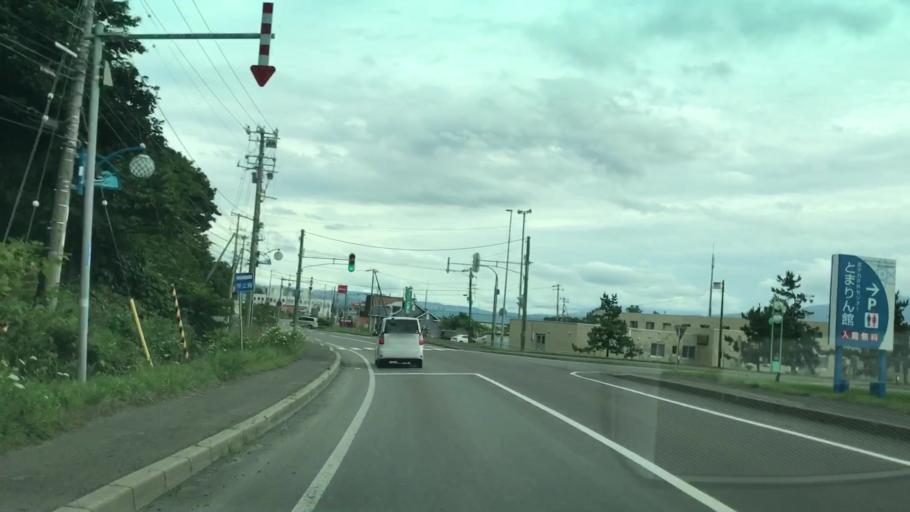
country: JP
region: Hokkaido
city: Iwanai
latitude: 43.0334
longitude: 140.5317
